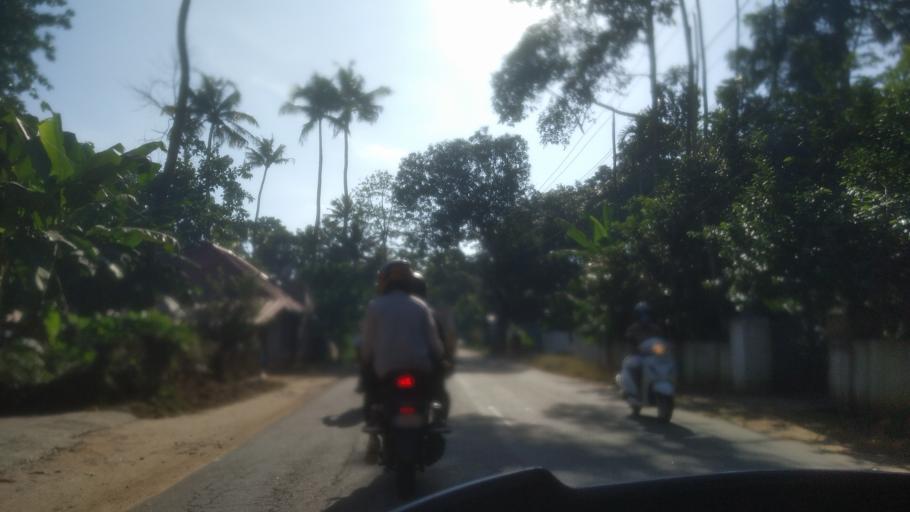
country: IN
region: Kerala
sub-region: Ernakulam
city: Ramamangalam
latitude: 9.9751
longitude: 76.5031
